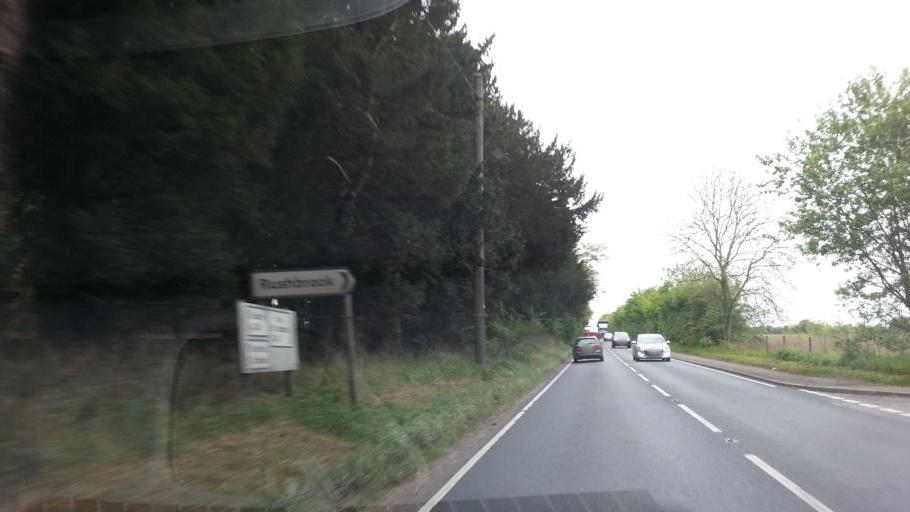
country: GB
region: England
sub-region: Suffolk
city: Bury St Edmunds
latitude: 52.2207
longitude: 0.7393
